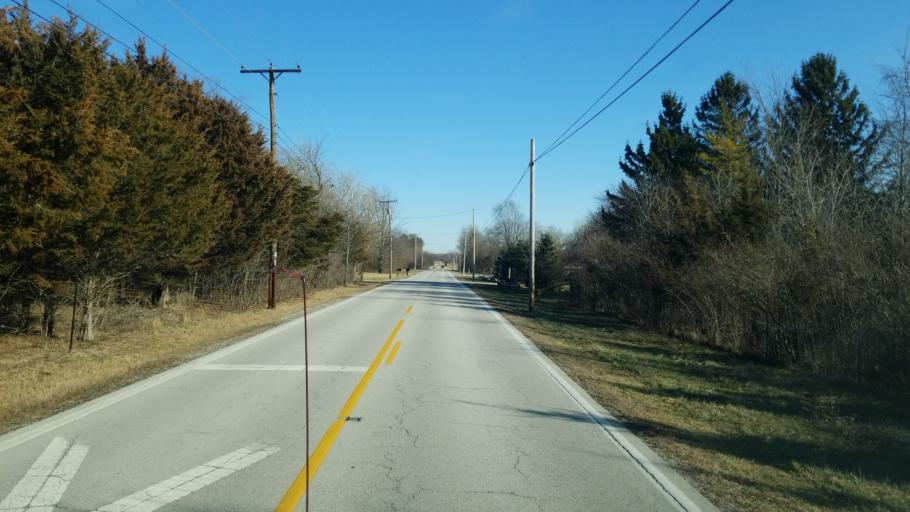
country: US
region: Ohio
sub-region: Wood County
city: Luckey
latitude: 41.4535
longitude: -83.4607
